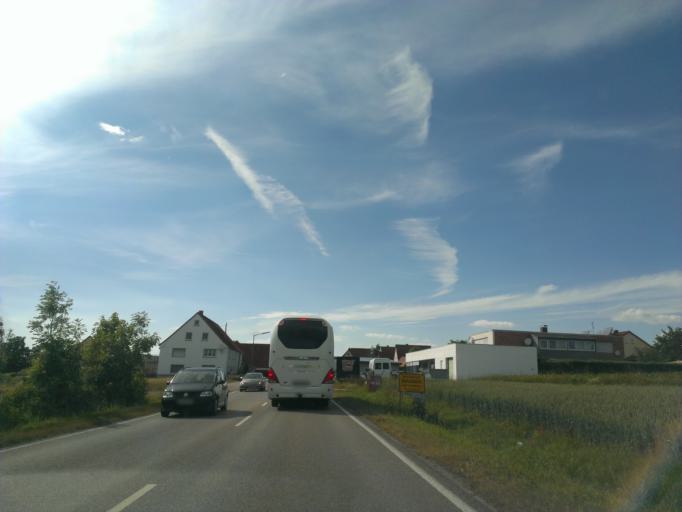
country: DE
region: Bavaria
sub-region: Regierungsbezirk Mittelfranken
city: Dinkelsbuhl
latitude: 49.0543
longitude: 10.3475
